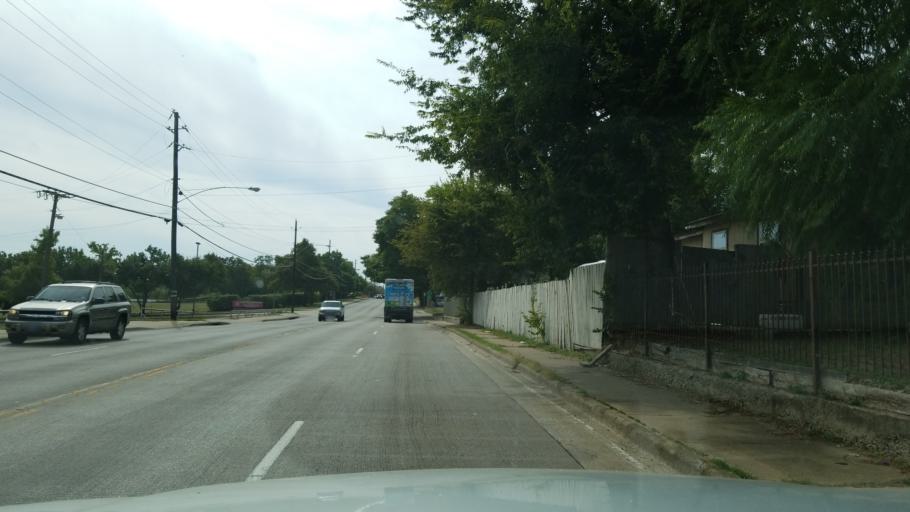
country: US
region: Texas
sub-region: Dallas County
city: Dallas
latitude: 32.7873
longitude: -96.7374
